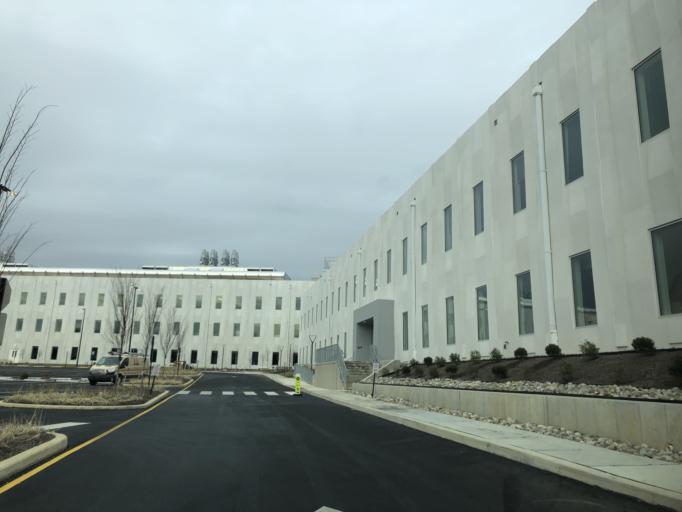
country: US
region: Delaware
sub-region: New Castle County
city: Newark
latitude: 39.6615
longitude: -75.7555
